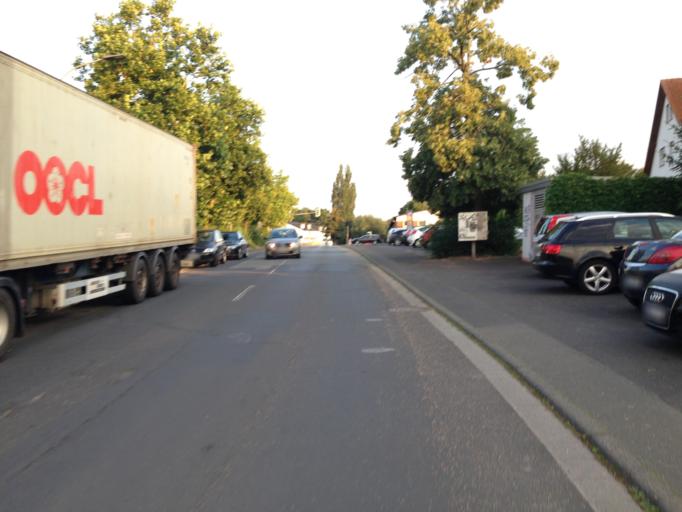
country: DE
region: Hesse
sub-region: Regierungsbezirk Giessen
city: Hoernsheim
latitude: 50.5258
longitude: 8.6475
